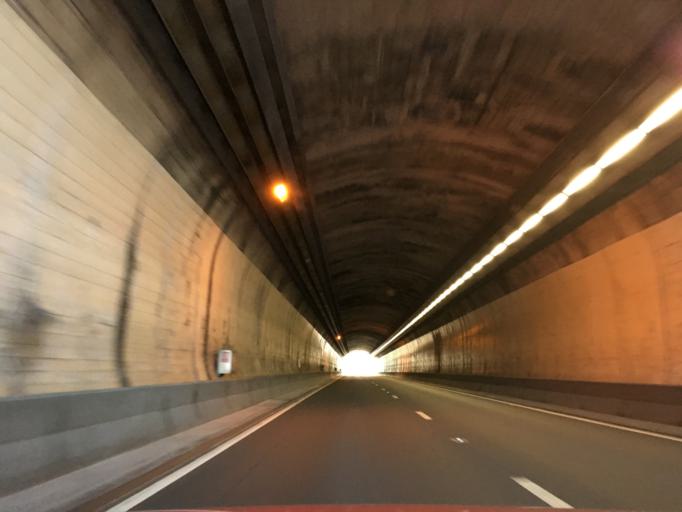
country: GB
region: Wales
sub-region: Monmouthshire
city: Monmouth
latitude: 51.8041
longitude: -2.7171
